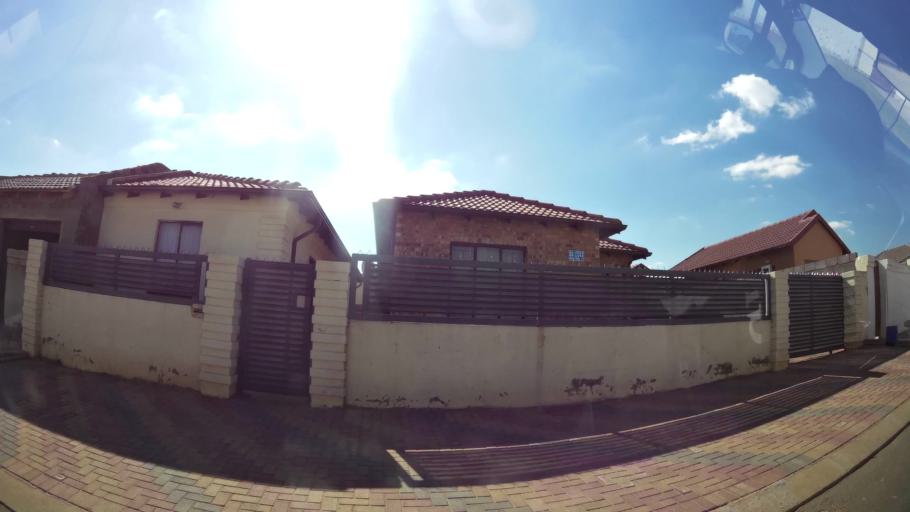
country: ZA
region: Gauteng
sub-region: West Rand District Municipality
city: Krugersdorp
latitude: -26.1512
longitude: 27.7751
